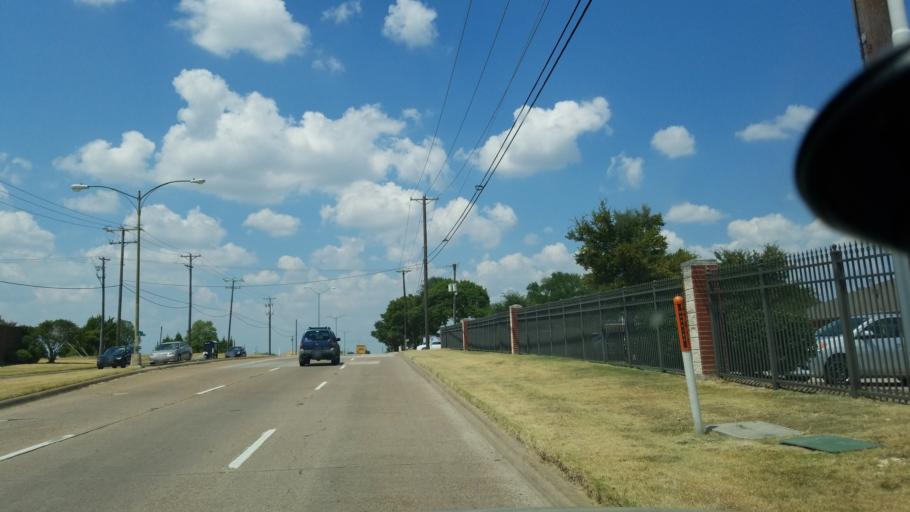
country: US
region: Texas
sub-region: Dallas County
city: Duncanville
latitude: 32.6777
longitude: -96.8827
